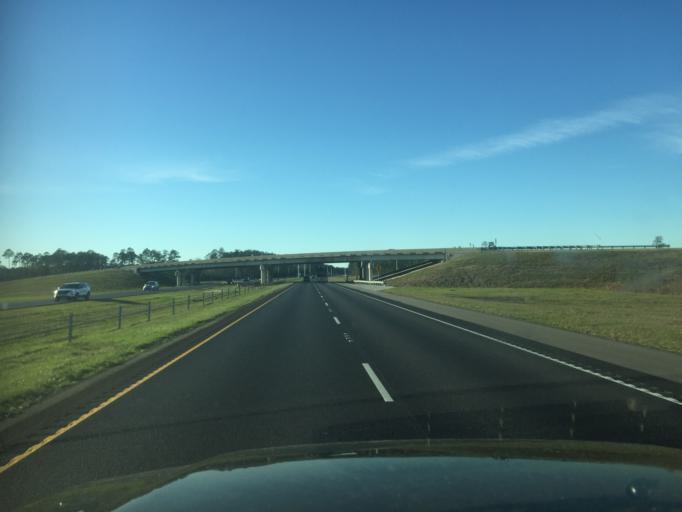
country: US
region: Louisiana
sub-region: Saint Tammany Parish
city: Mandeville
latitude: 30.3920
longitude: -90.0014
